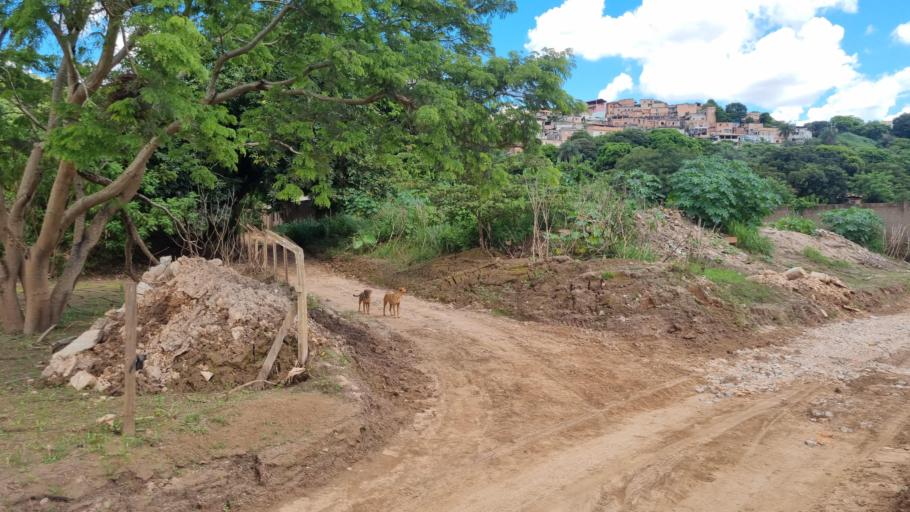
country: BR
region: Minas Gerais
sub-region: Santa Luzia
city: Santa Luzia
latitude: -19.8341
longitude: -43.8654
